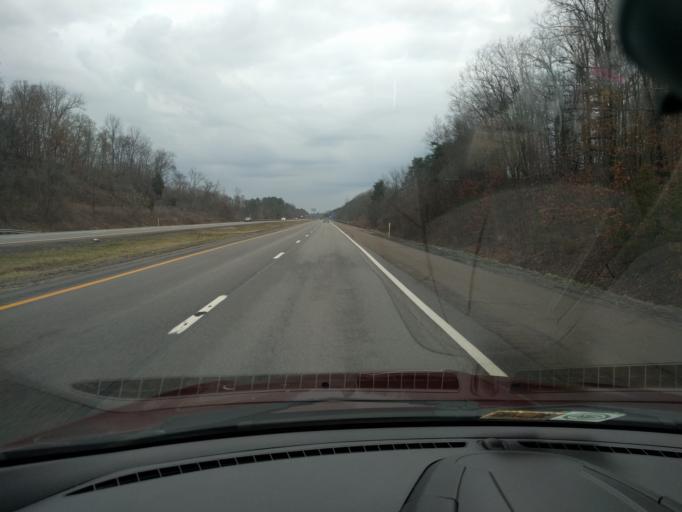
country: US
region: West Virginia
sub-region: Wood County
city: Williamstown
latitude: 39.3598
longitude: -81.4417
